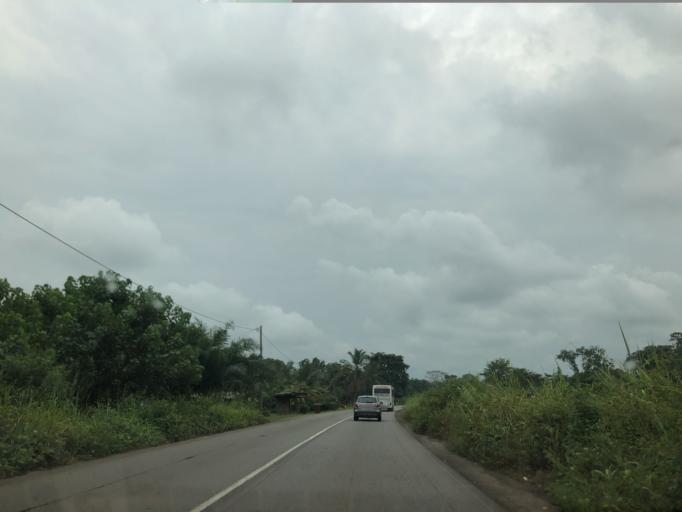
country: CM
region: Littoral
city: Edea
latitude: 3.4725
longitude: 10.1340
